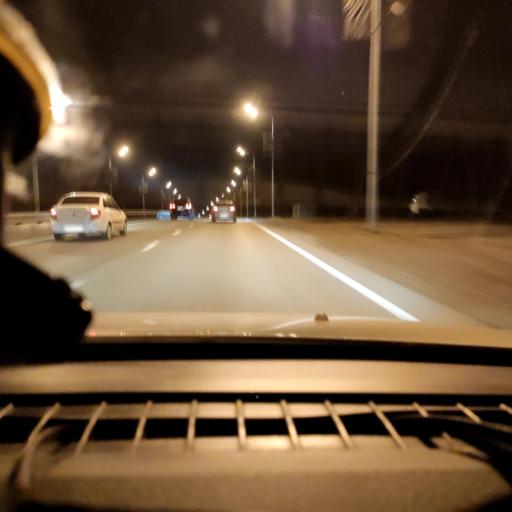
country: RU
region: Samara
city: Novosemeykino
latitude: 53.3202
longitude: 50.2302
